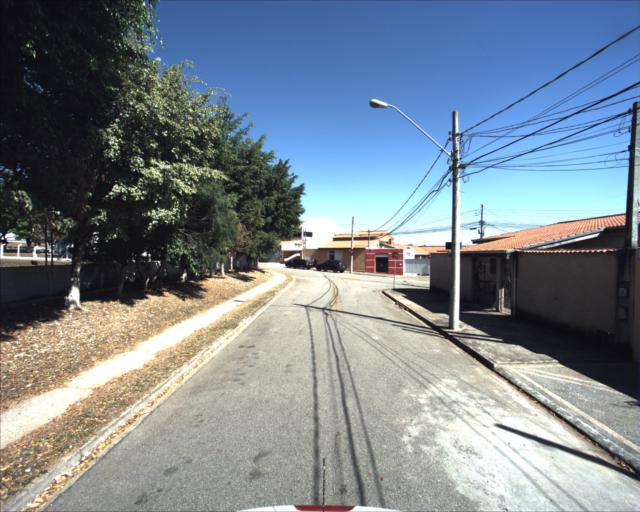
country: BR
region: Sao Paulo
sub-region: Sorocaba
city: Sorocaba
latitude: -23.4922
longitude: -47.4209
